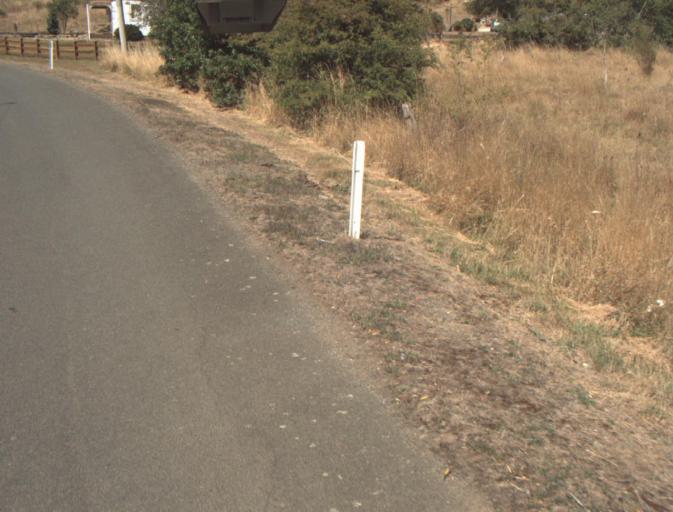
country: AU
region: Tasmania
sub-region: Launceston
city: Newstead
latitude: -41.3883
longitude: 147.2965
